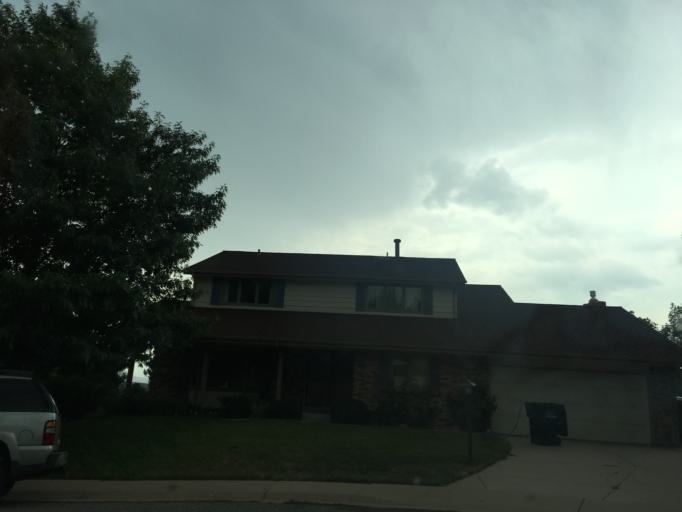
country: US
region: Colorado
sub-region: Arapahoe County
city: Sheridan
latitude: 39.6625
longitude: -105.0330
